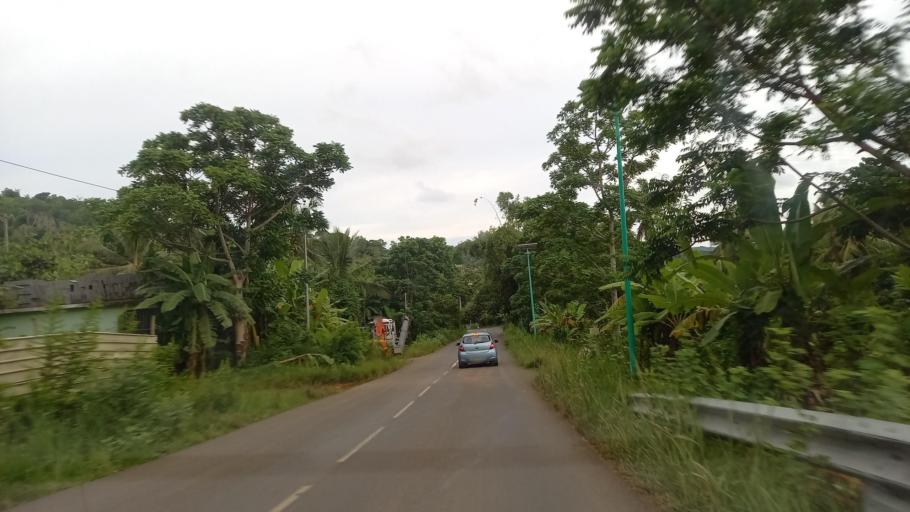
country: YT
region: Ouangani
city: Ouangani
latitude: -12.8897
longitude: 45.1373
